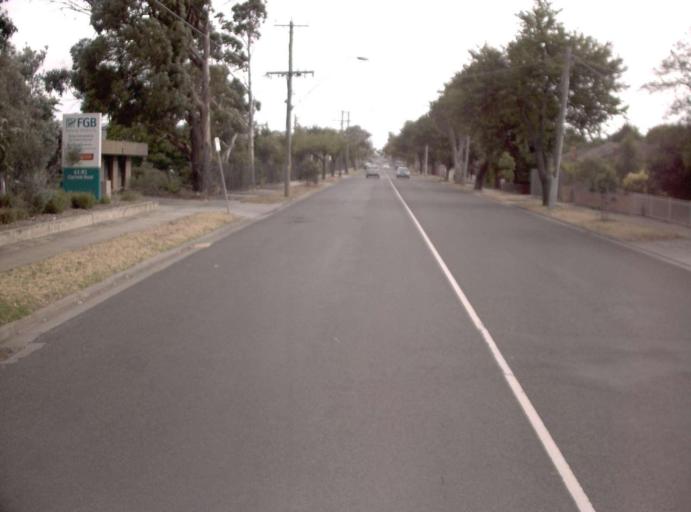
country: AU
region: Victoria
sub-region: Monash
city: Oakleigh South
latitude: -37.9327
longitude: 145.0995
